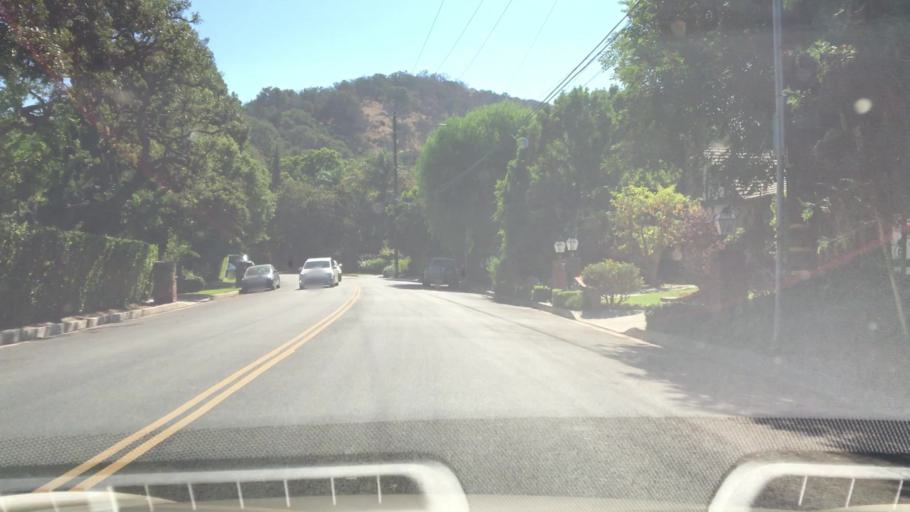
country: US
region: California
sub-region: Los Angeles County
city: Sherman Oaks
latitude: 34.1441
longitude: -118.4425
